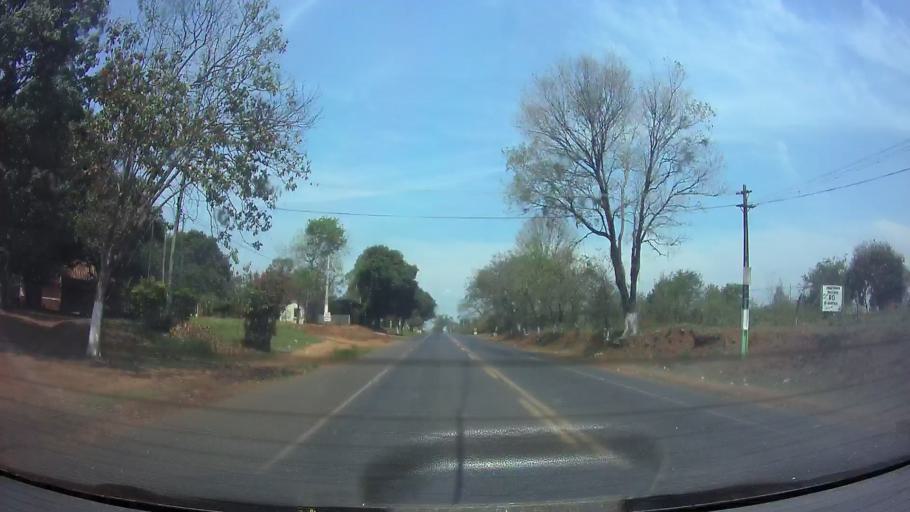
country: PY
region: Central
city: Guarambare
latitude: -25.4559
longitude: -57.4312
